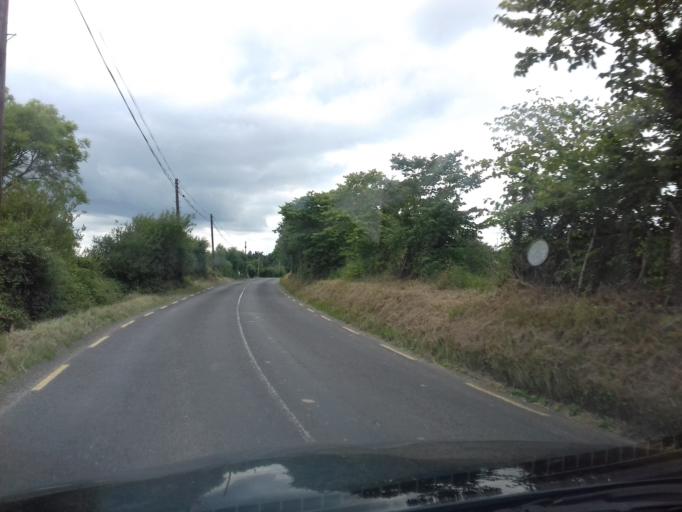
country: IE
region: Leinster
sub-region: Loch Garman
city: Castlebridge
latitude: 52.3897
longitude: -6.4089
